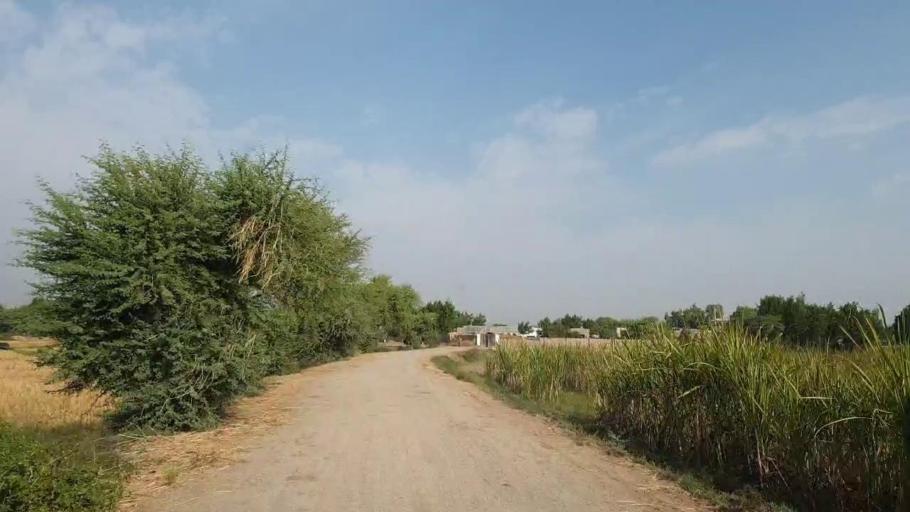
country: PK
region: Sindh
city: Tando Muhammad Khan
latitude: 25.0501
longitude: 68.4358
